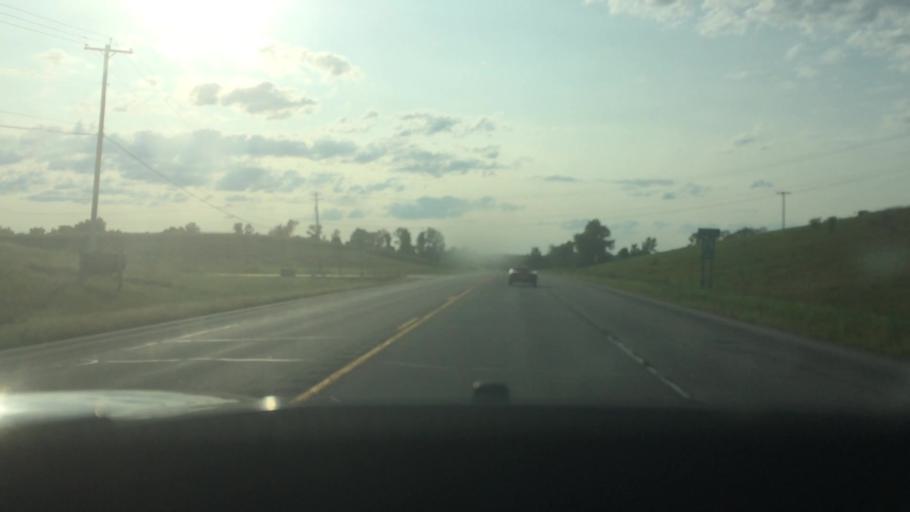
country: US
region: New York
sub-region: St. Lawrence County
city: Canton
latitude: 44.6338
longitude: -75.2538
